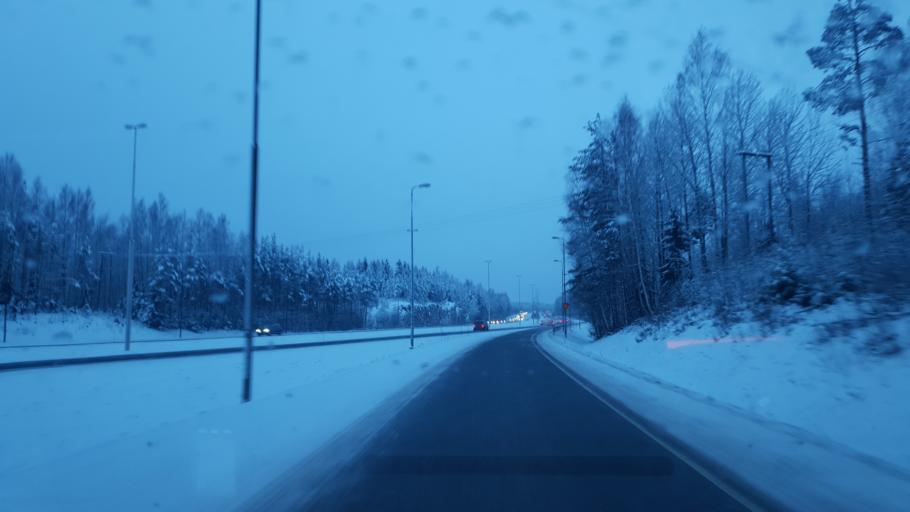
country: FI
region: Uusimaa
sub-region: Helsinki
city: Kerava
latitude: 60.3846
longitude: 25.1171
